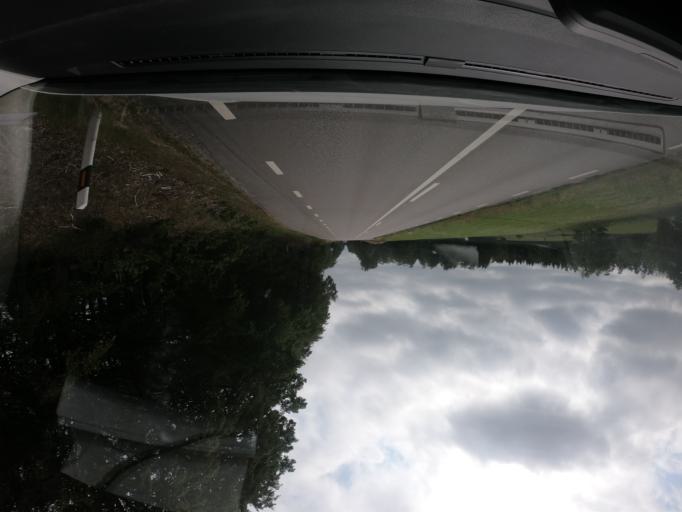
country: SE
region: Skane
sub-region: Perstorps Kommun
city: Perstorp
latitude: 56.2410
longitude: 13.4963
